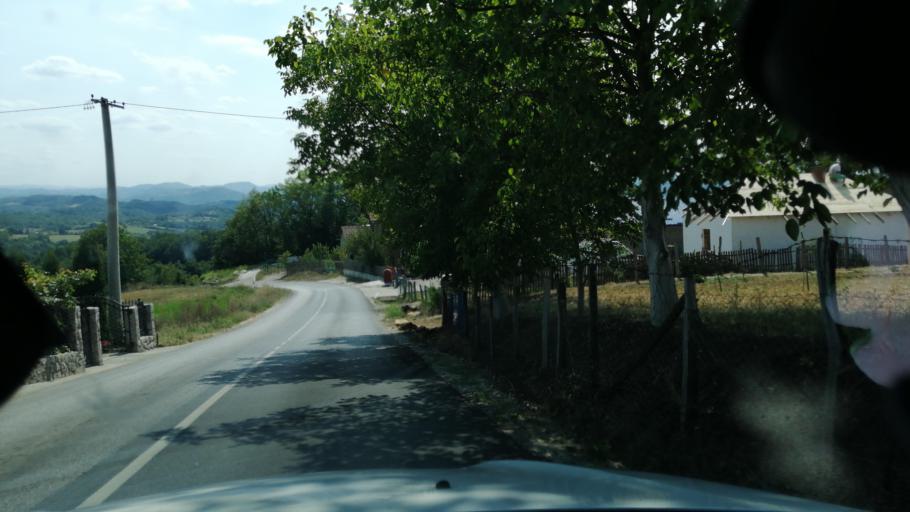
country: RS
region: Central Serbia
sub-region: Moravicki Okrug
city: Cacak
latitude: 43.8190
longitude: 20.2782
